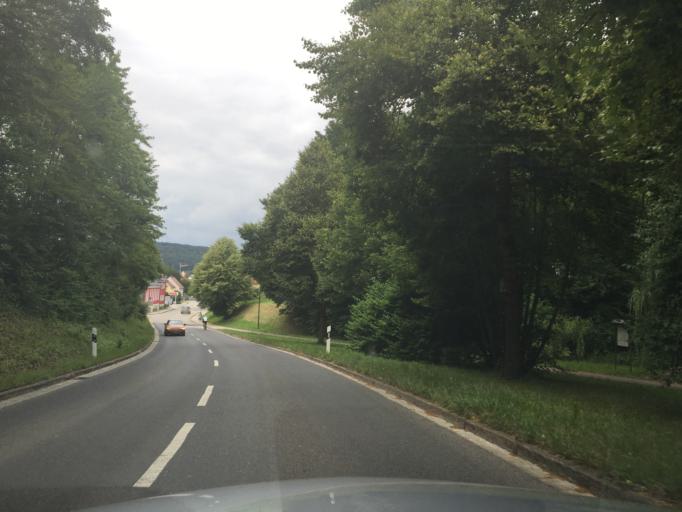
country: DE
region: Bavaria
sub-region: Regierungsbezirk Mittelfranken
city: Greding
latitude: 49.0450
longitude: 11.3611
